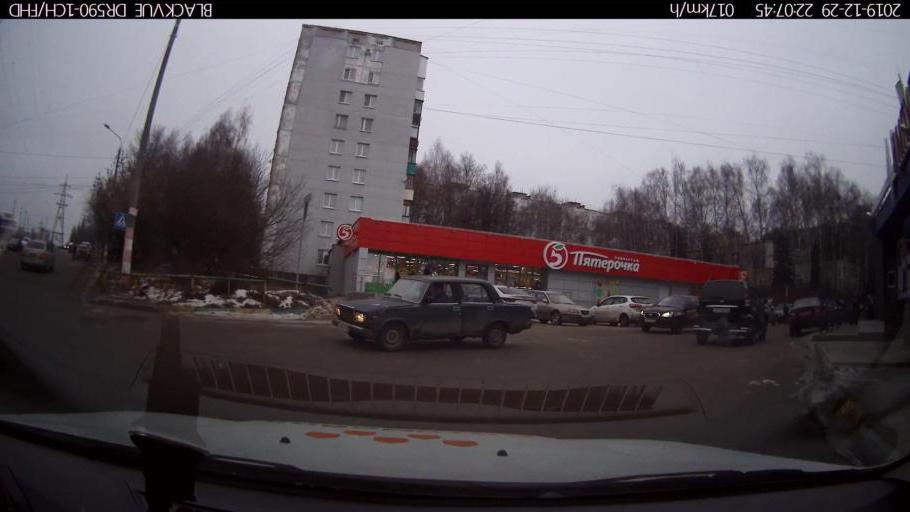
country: RU
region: Nizjnij Novgorod
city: Nizhniy Novgorod
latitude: 56.2288
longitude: 43.9482
